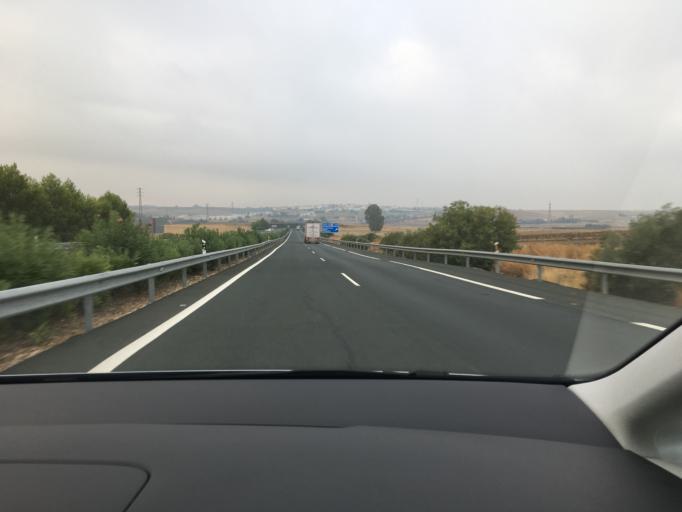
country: ES
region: Andalusia
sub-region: Province of Cordoba
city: La Carlota
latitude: 37.6907
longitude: -4.9218
